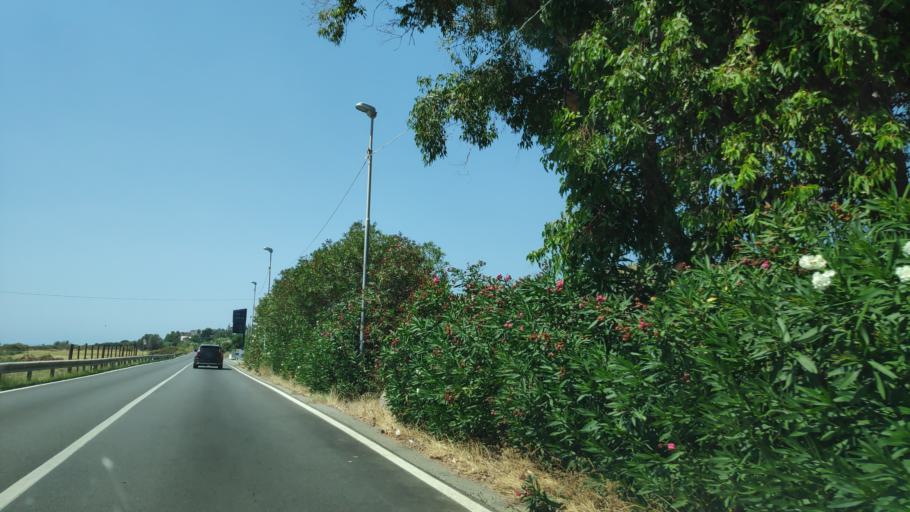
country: IT
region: Calabria
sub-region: Provincia di Reggio Calabria
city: Weather Station
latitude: 37.9439
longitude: 16.0826
